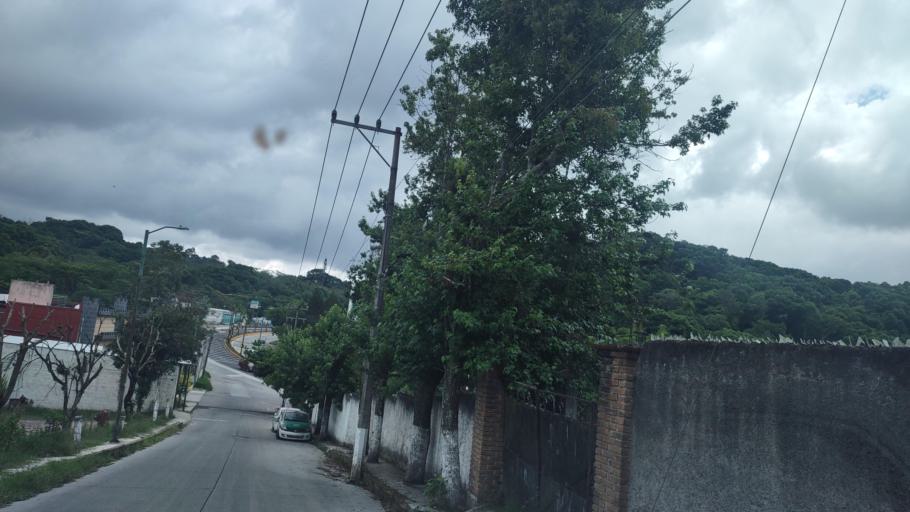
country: MX
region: Veracruz
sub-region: Xalapa
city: Xalapa de Enriquez
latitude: 19.5089
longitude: -96.9362
